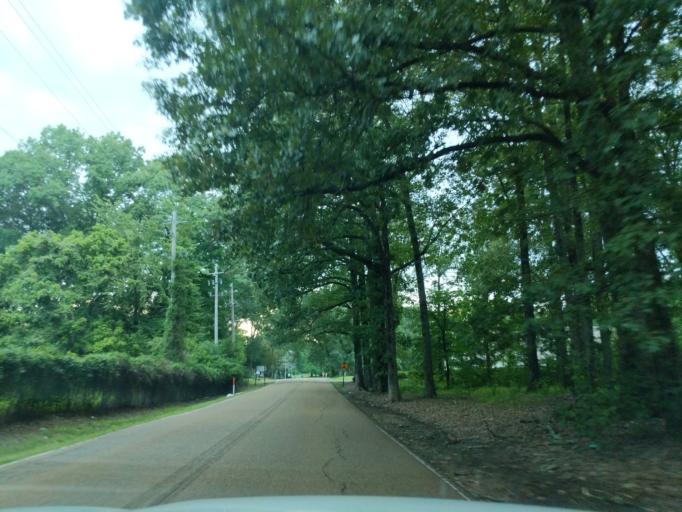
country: US
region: Tennessee
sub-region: Shelby County
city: Germantown
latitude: 35.0777
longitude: -89.8273
